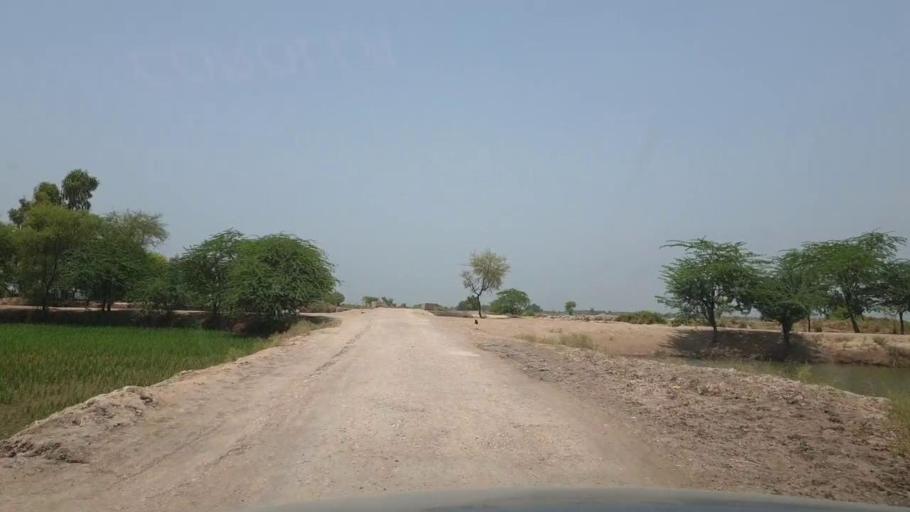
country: PK
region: Sindh
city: Garhi Yasin
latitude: 27.8782
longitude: 68.4453
